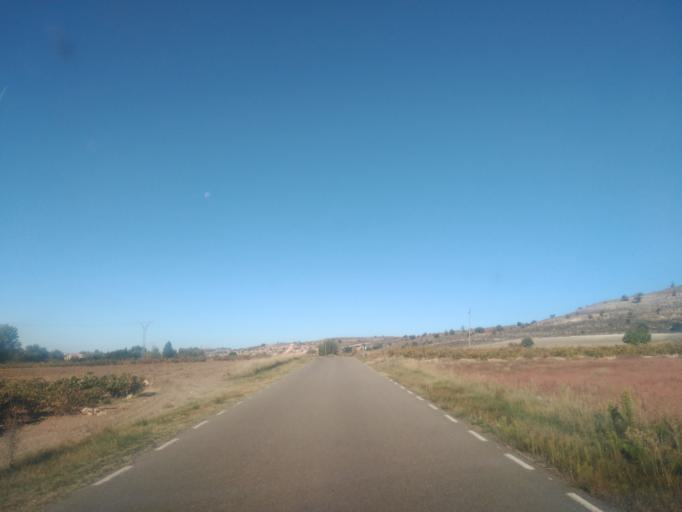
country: ES
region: Castille and Leon
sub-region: Provincia de Burgos
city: Penaranda de Duero
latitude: 41.6859
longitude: -3.4370
